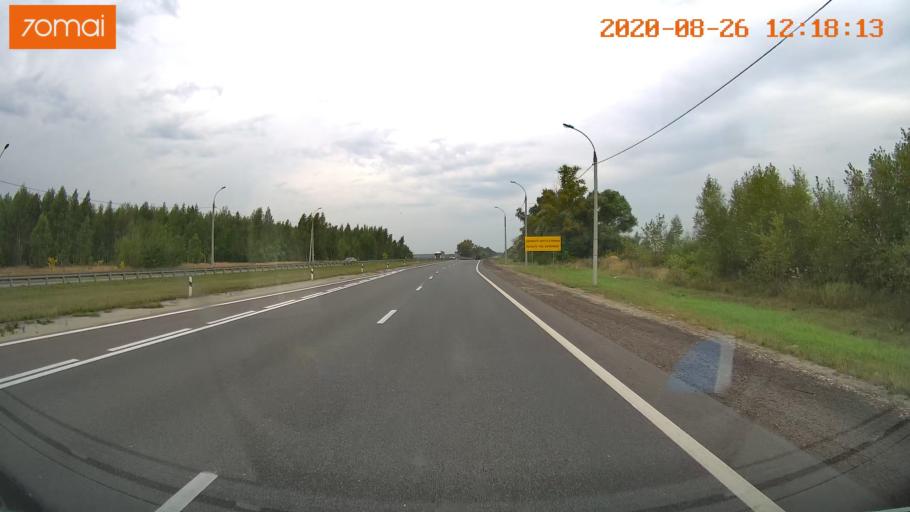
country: RU
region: Rjazan
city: Murmino
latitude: 54.4708
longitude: 40.0218
